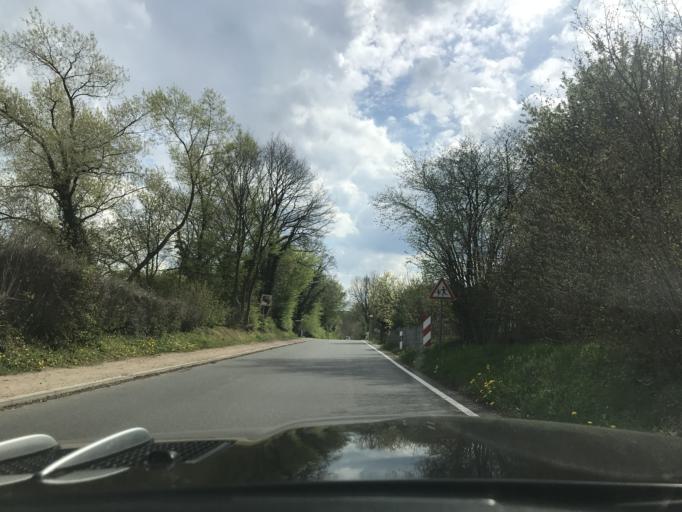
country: DE
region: Schleswig-Holstein
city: Ratekau
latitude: 53.9334
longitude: 10.7838
